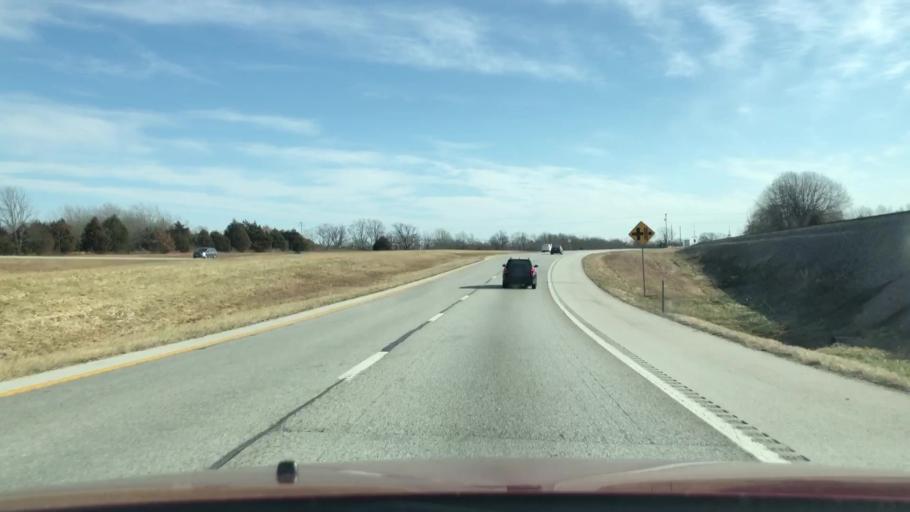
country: US
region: Missouri
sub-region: Webster County
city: Seymour
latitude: 37.1311
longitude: -92.7229
